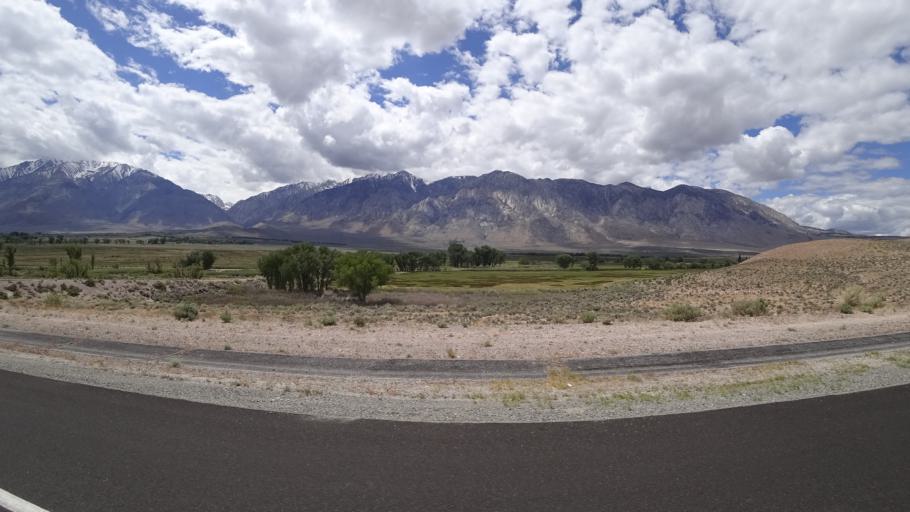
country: US
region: California
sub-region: Inyo County
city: West Bishop
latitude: 37.4470
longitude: -118.5726
